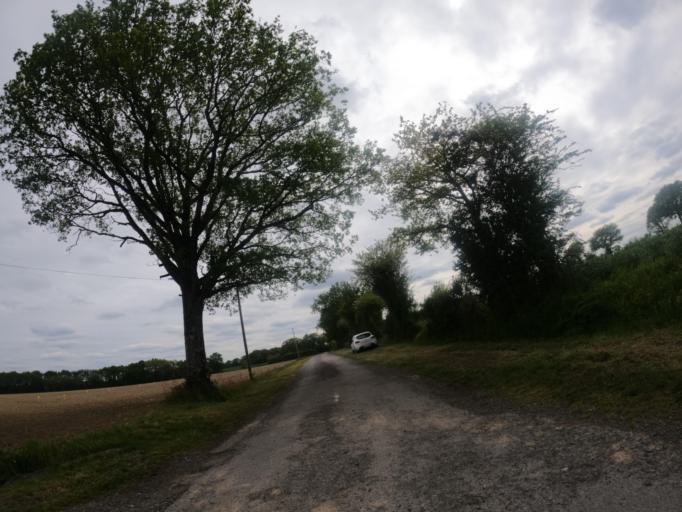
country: FR
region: Pays de la Loire
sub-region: Departement de la Loire-Atlantique
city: Chateaubriant
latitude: 47.7326
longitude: -1.4118
